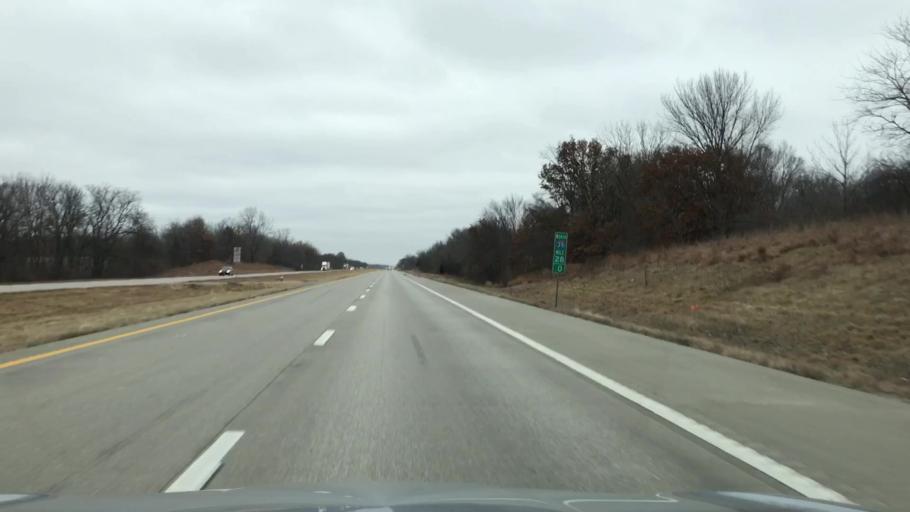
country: US
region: Missouri
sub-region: Clay County
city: Kearney
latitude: 39.3922
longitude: -94.3590
